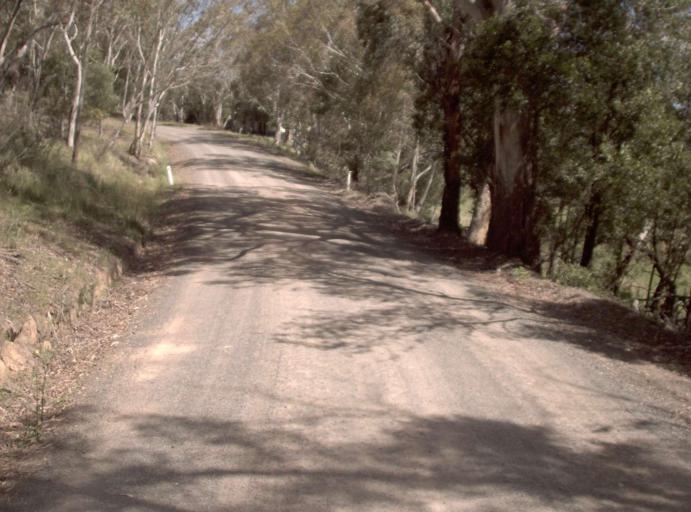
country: AU
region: New South Wales
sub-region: Bombala
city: Bombala
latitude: -37.1527
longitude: 148.6707
